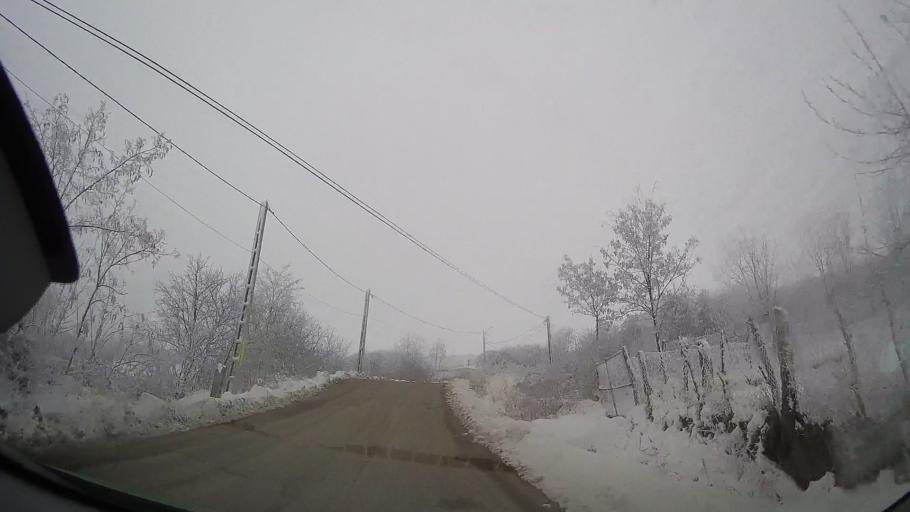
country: RO
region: Iasi
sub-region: Comuna Tibanesti
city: Tibanesti
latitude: 46.8948
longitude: 27.3084
